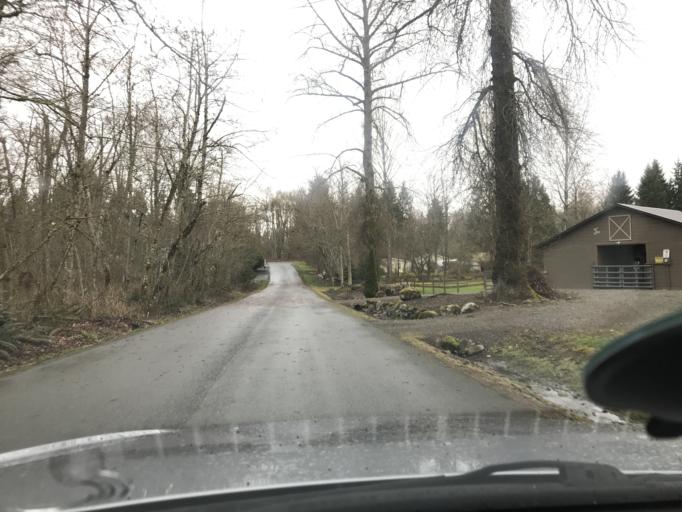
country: US
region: Washington
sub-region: King County
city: Ames Lake
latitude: 47.6479
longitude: -121.9894
